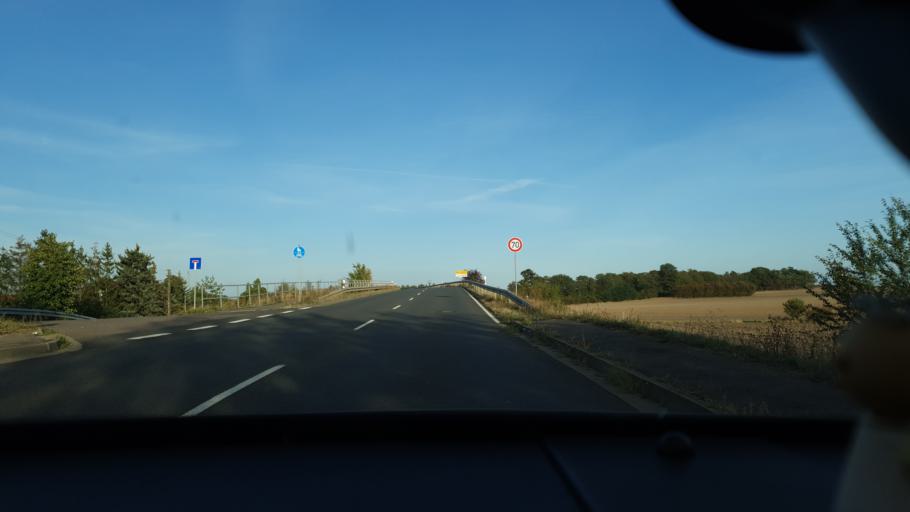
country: DE
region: Saxony
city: Jesewitz
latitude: 51.4585
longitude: 12.5791
